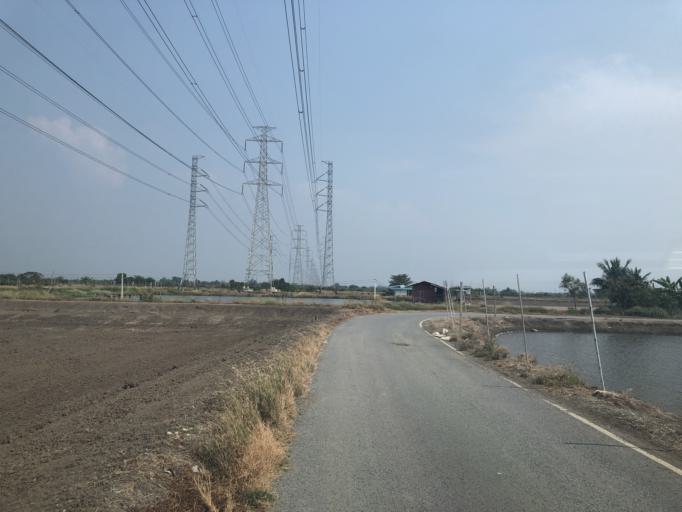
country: TH
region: Samut Prakan
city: Bang Bo
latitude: 13.5420
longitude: 100.8880
